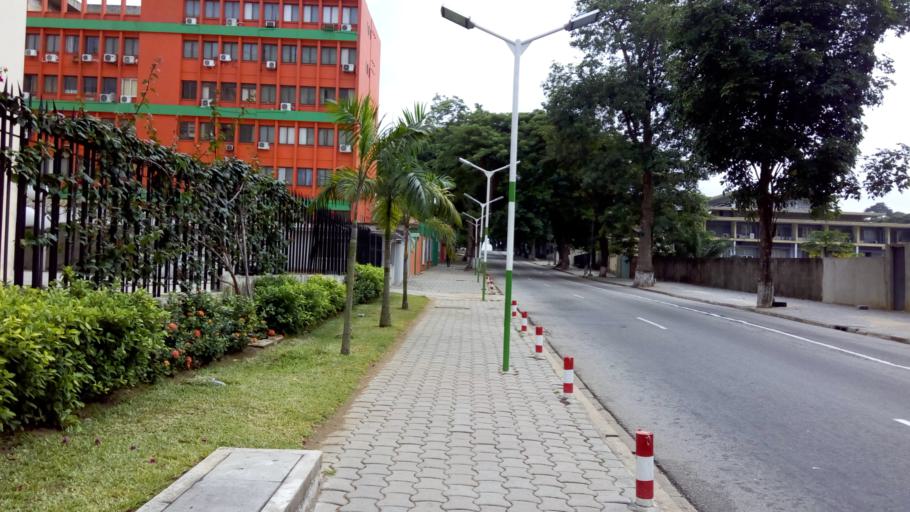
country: CI
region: Lagunes
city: Abidjan
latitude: 5.3276
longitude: -4.0208
